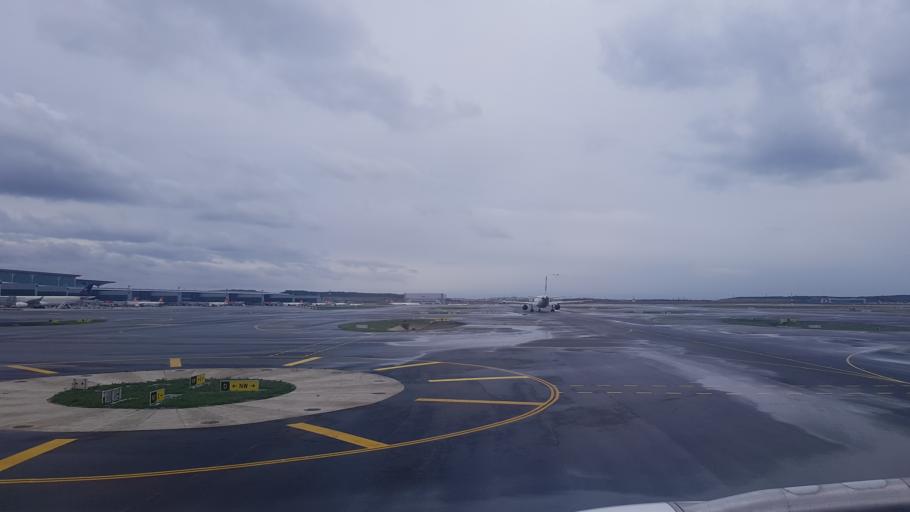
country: TR
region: Istanbul
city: Durusu
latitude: 41.2696
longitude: 28.7314
